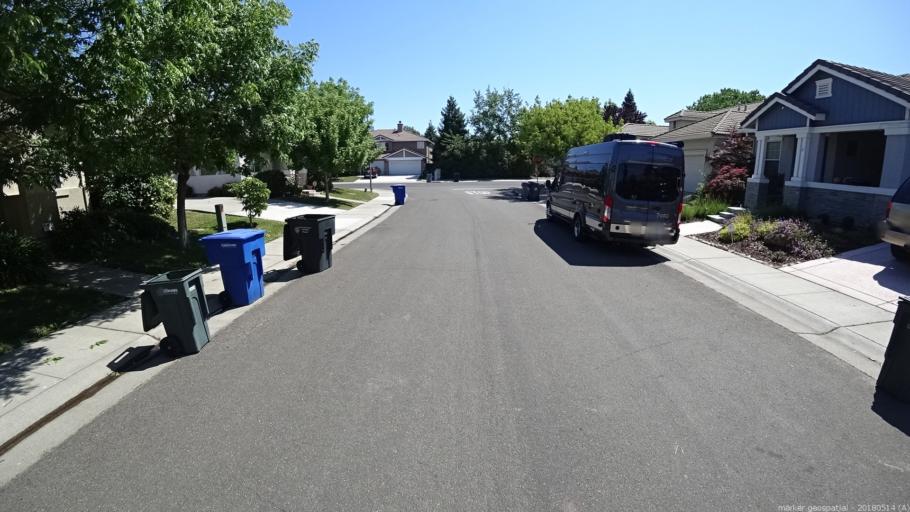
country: US
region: California
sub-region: Yolo County
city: West Sacramento
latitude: 38.6381
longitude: -121.5348
